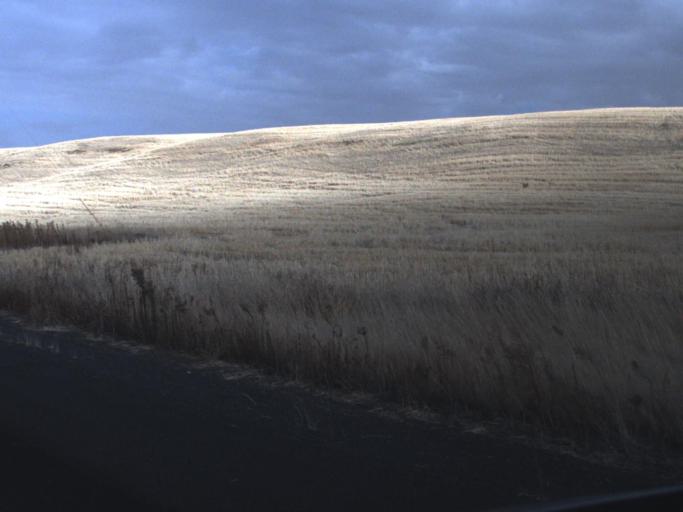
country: US
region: Washington
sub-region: Lincoln County
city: Davenport
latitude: 47.5149
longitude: -118.2179
